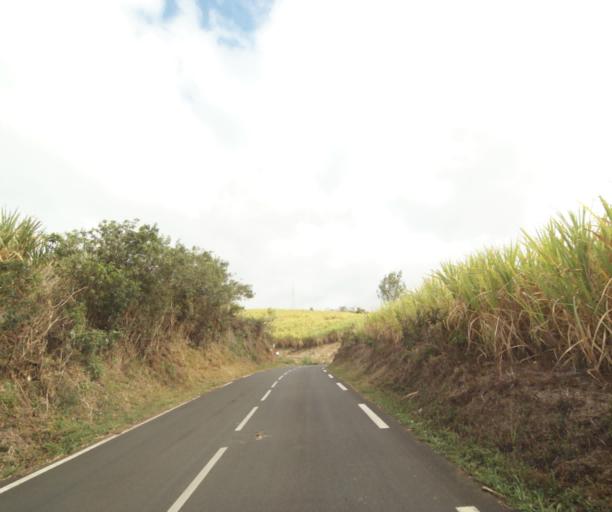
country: RE
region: Reunion
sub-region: Reunion
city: Saint-Paul
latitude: -21.0252
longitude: 55.3142
